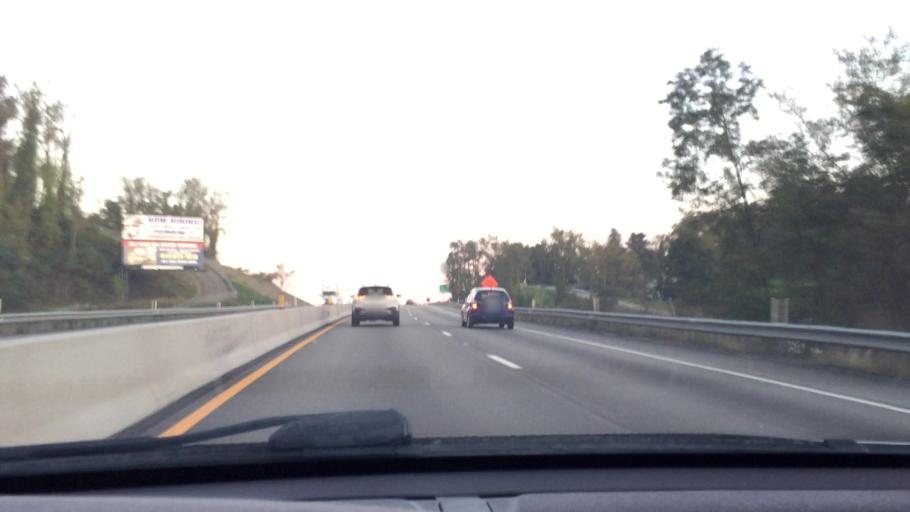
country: US
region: Pennsylvania
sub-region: Washington County
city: North Charleroi
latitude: 40.1203
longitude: -79.9528
